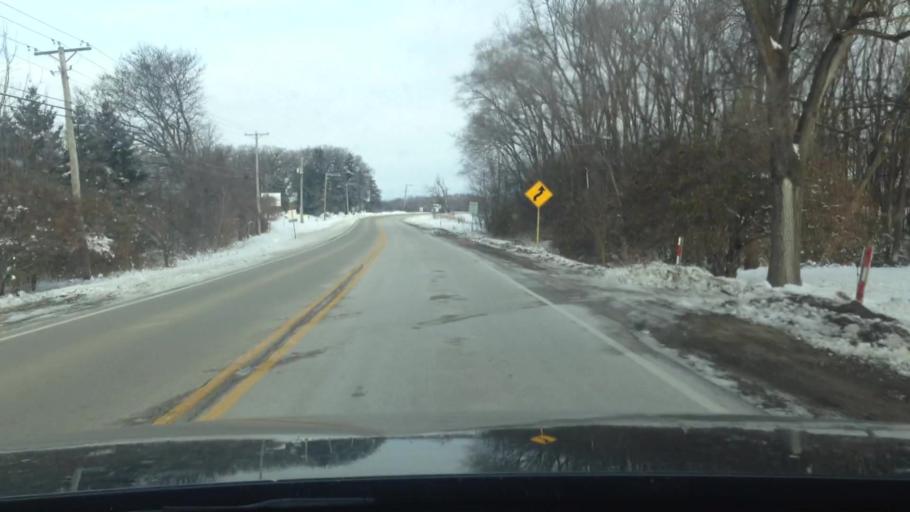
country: US
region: Illinois
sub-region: McHenry County
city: Woodstock
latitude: 42.3468
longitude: -88.4437
